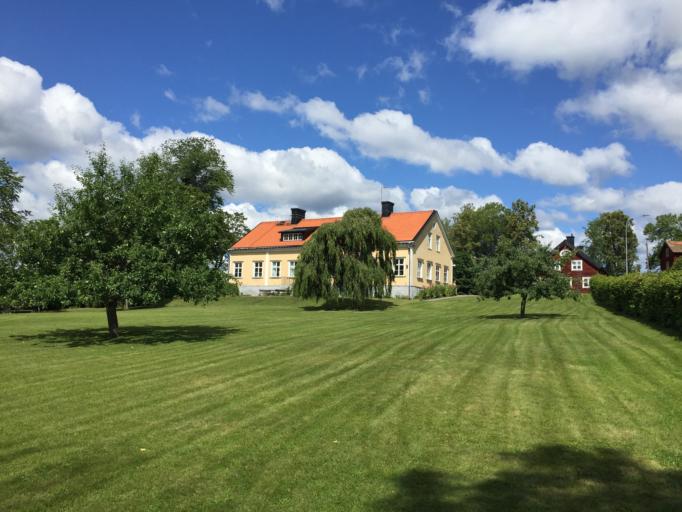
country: SE
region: OEstergoetland
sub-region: Finspangs Kommun
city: Finspang
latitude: 58.6746
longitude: 15.8432
